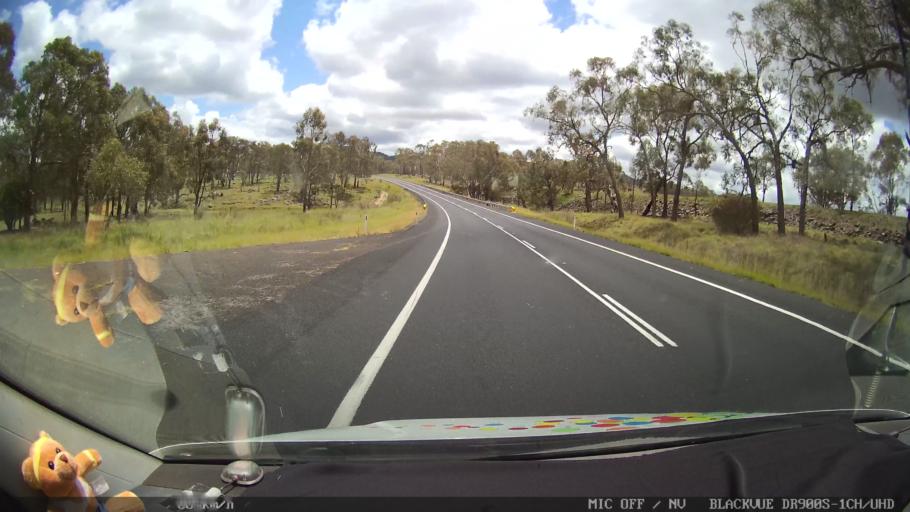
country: AU
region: New South Wales
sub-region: Glen Innes Severn
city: Glen Innes
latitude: -29.3682
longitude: 151.8973
